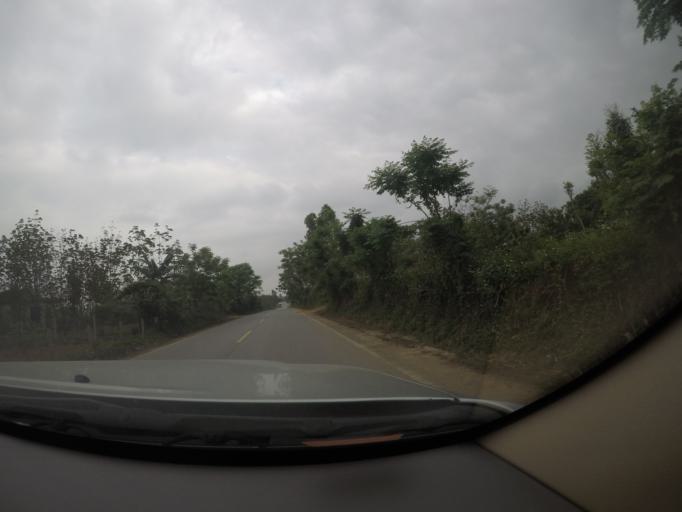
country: VN
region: Quang Binh
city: Hoan Lao
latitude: 17.5806
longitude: 106.4363
